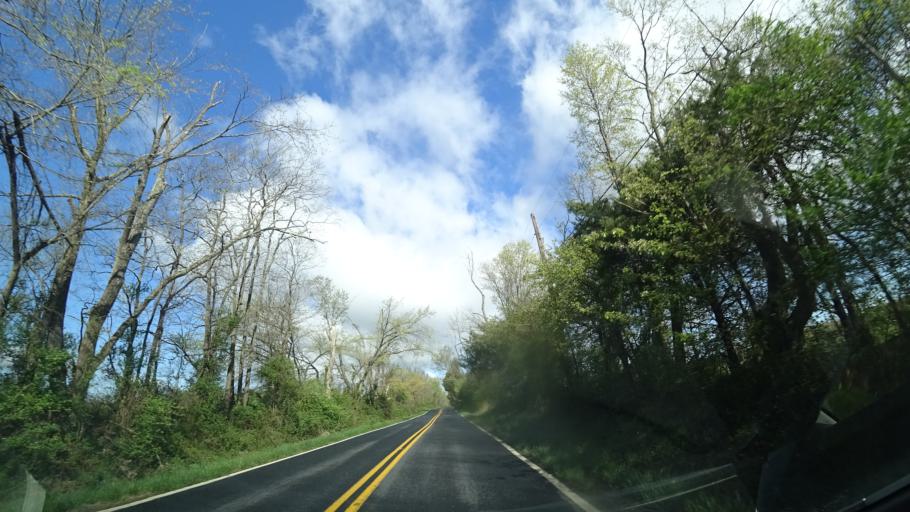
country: US
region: Virginia
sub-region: Loudoun County
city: Lowes Island
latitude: 39.0841
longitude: -77.3558
